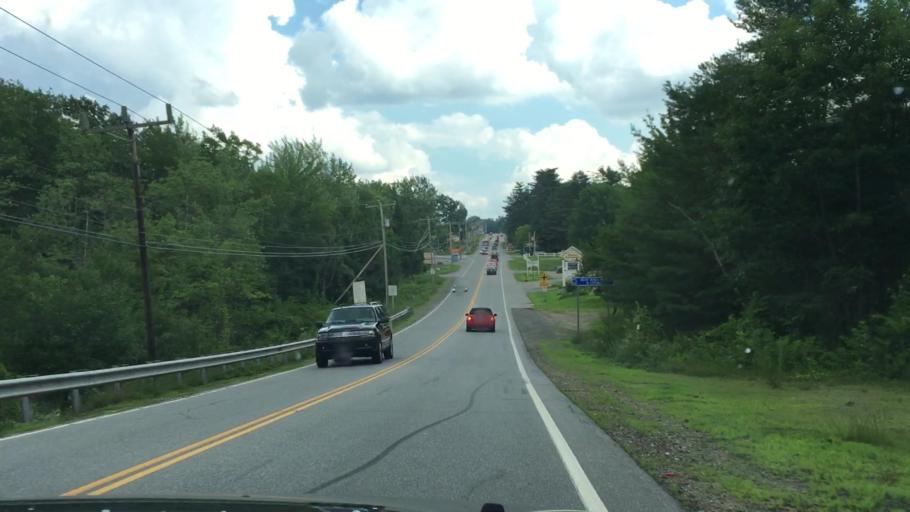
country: US
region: New Hampshire
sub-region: Belknap County
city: Meredith
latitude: 43.6195
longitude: -71.4828
